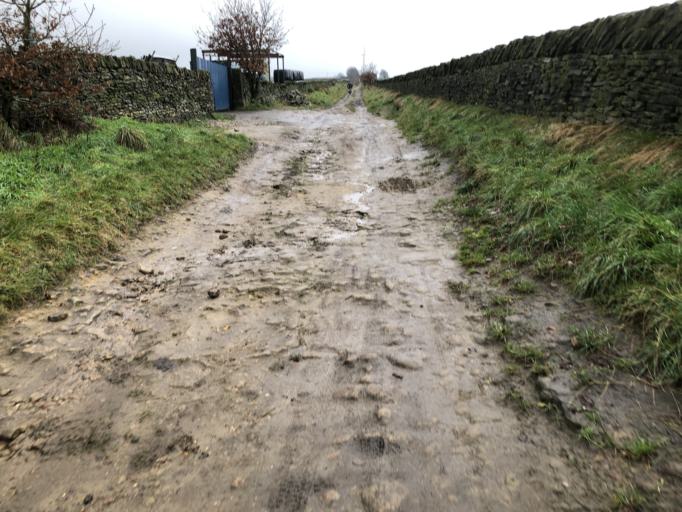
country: GB
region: England
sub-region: Kirklees
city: Holmfirth
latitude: 53.5590
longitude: -1.7739
